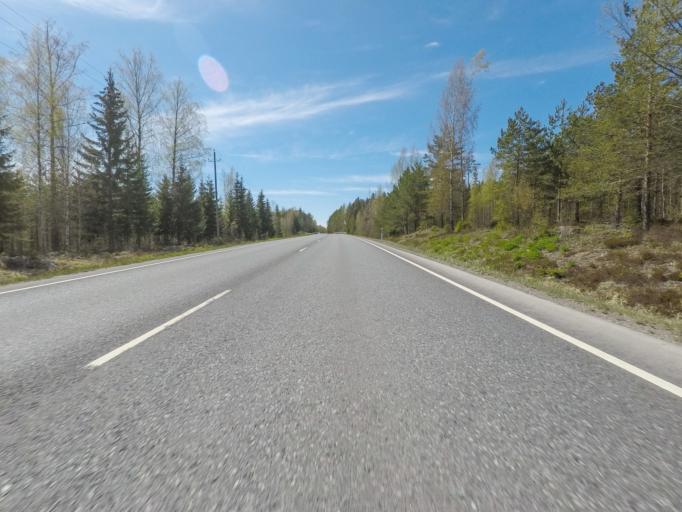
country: FI
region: Haeme
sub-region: Forssa
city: Humppila
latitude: 60.9847
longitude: 23.4461
